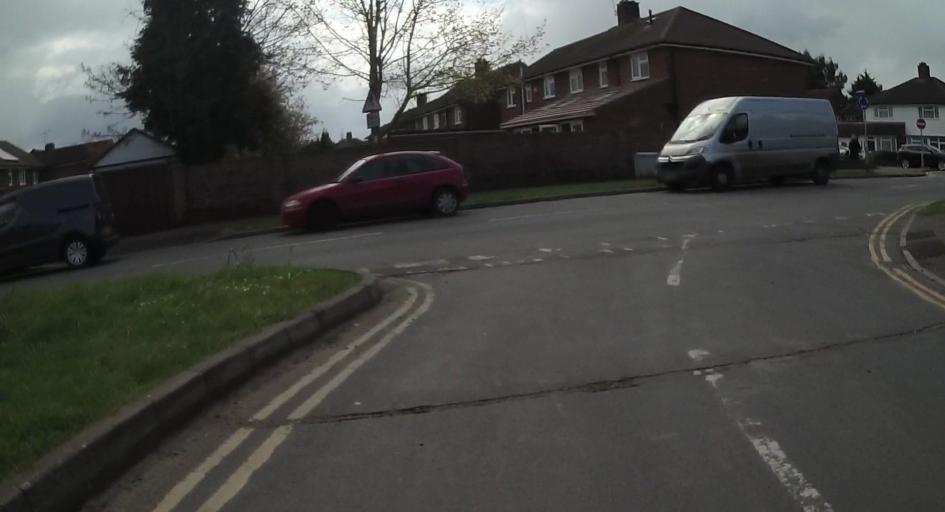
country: GB
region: England
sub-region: Surrey
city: West Byfleet
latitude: 51.3500
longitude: -0.5048
